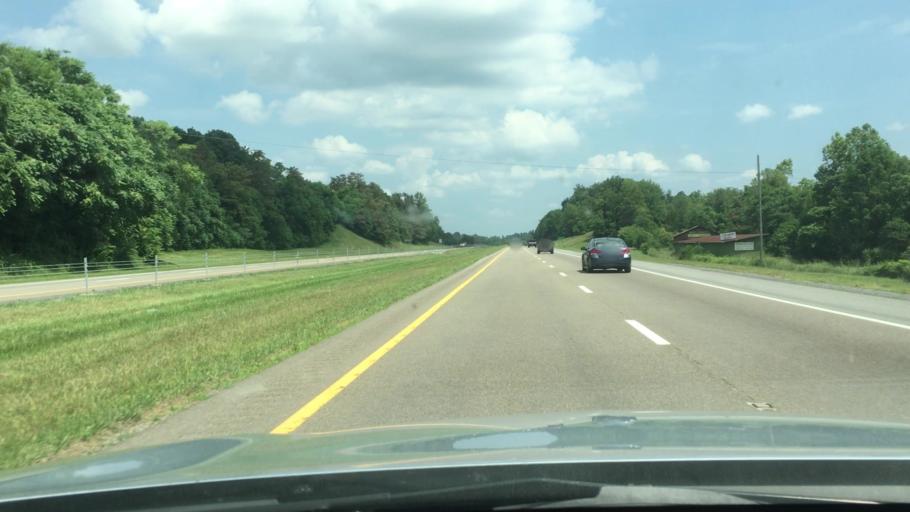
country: US
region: Tennessee
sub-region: Carter County
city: Pine Crest
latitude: 36.2569
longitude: -82.3227
